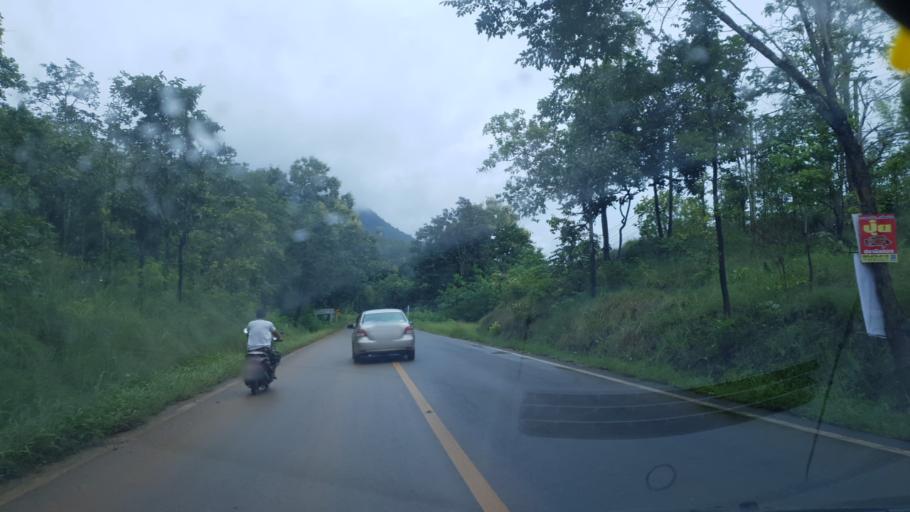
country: TH
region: Mae Hong Son
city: Pa Pae
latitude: 18.1988
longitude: 97.9375
